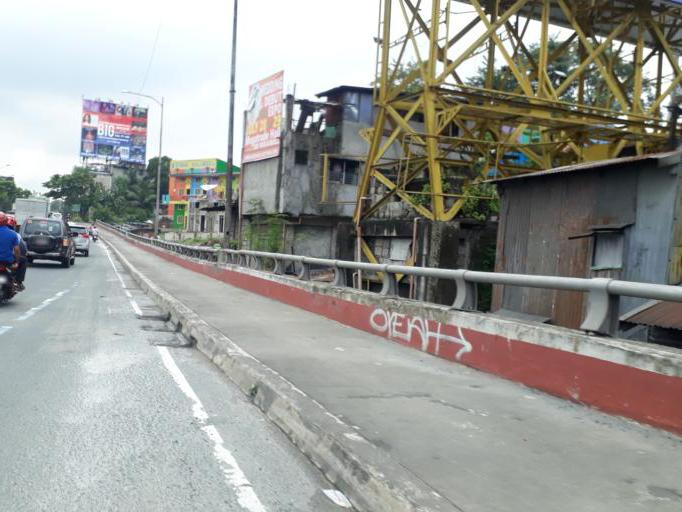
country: PH
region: Metro Manila
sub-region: Marikina
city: Calumpang
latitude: 14.6277
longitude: 121.0741
